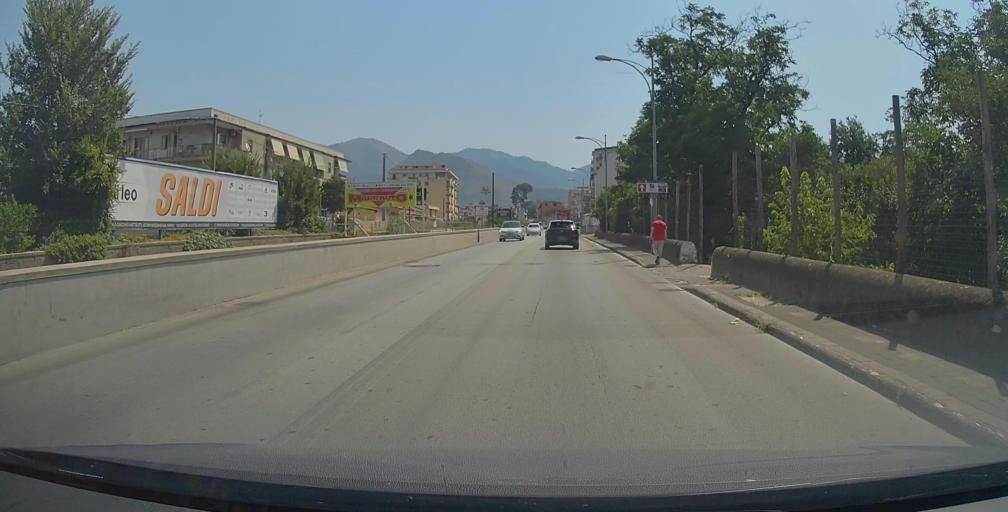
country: IT
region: Campania
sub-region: Provincia di Salerno
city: Nocera Superiore
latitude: 40.7406
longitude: 14.6587
